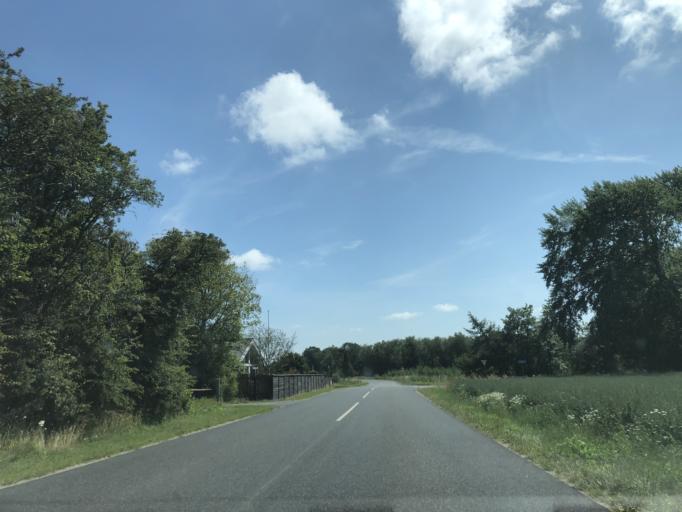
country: DK
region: Central Jutland
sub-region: Favrskov Kommune
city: Ulstrup
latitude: 56.3061
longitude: 9.7646
